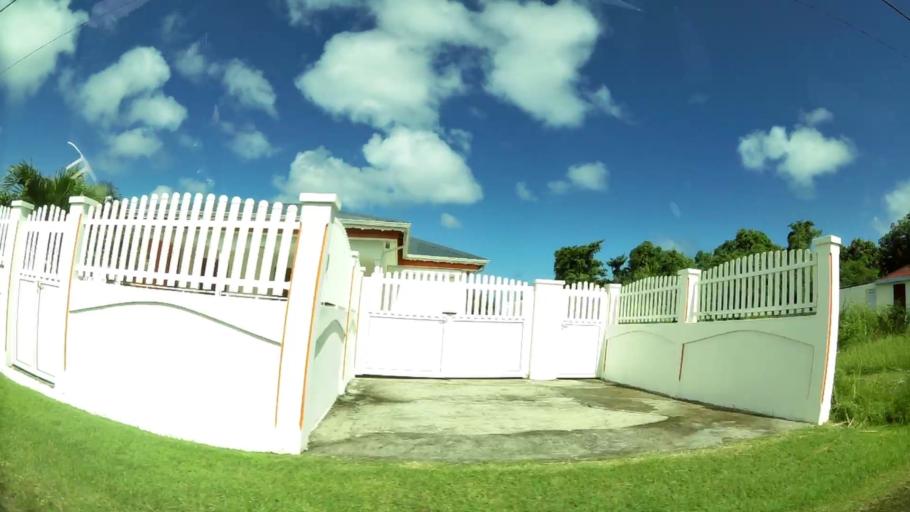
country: GP
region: Guadeloupe
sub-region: Guadeloupe
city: Anse-Bertrand
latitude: 16.4700
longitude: -61.5050
